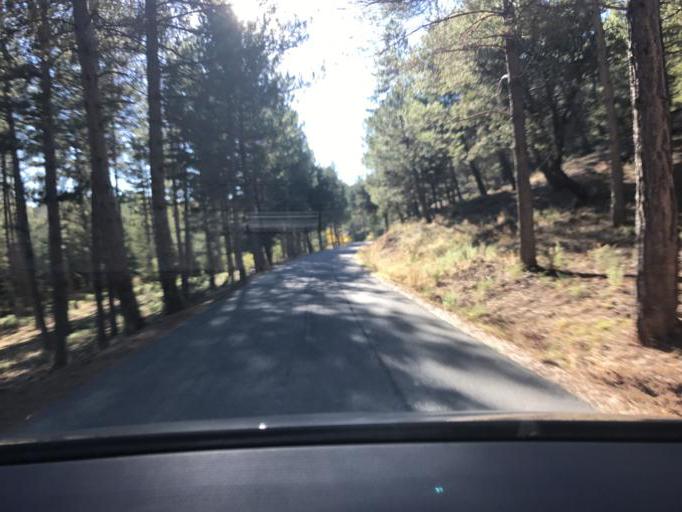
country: ES
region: Andalusia
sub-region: Provincia de Granada
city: Beas de Granada
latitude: 37.3057
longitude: -3.4572
